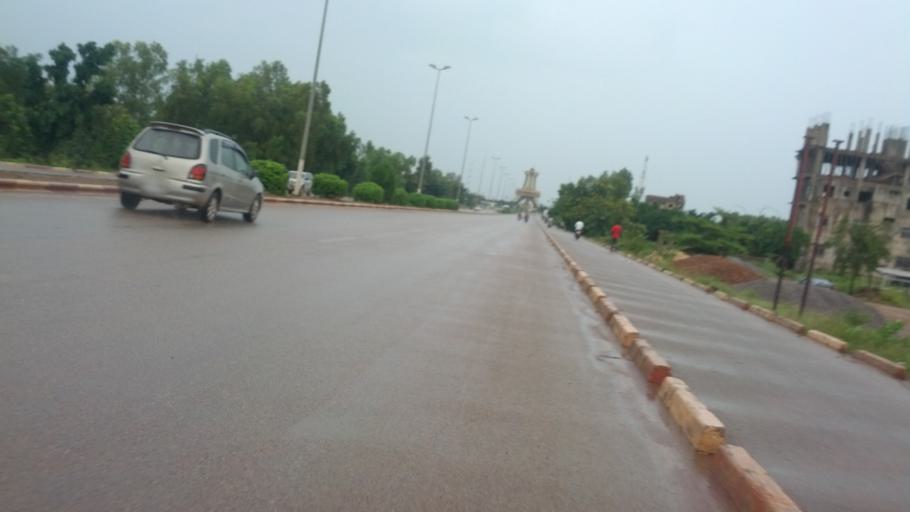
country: BF
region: Centre
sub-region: Kadiogo Province
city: Ouagadougou
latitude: 12.3215
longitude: -1.5027
